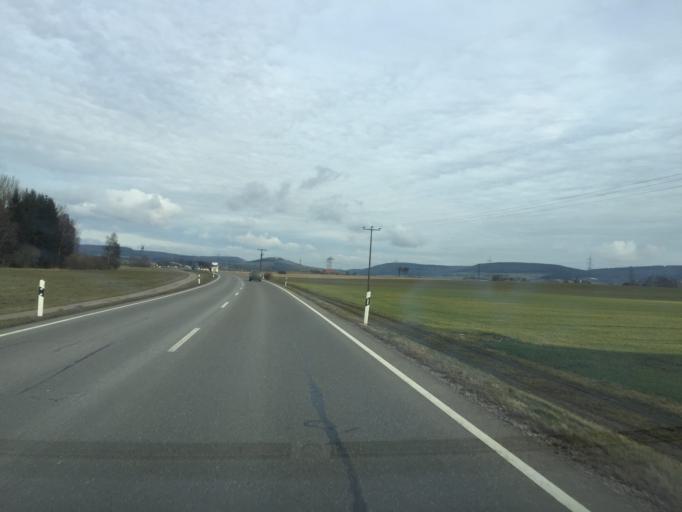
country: DE
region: Baden-Wuerttemberg
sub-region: Freiburg Region
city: Hufingen
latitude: 47.9242
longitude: 8.5210
